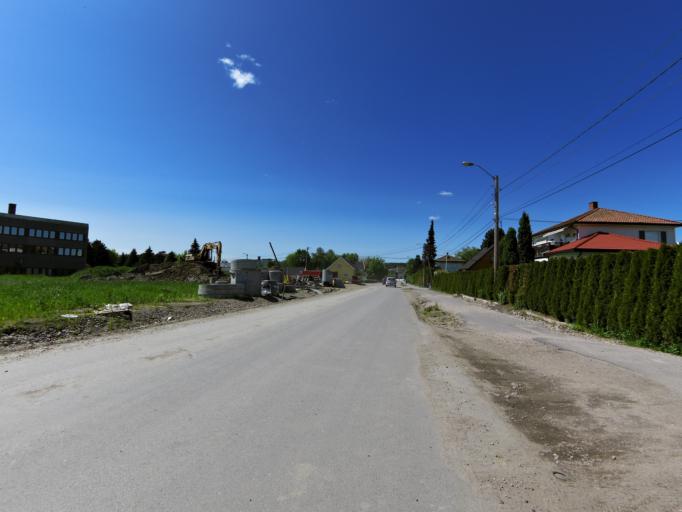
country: NO
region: Ostfold
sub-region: Fredrikstad
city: Fredrikstad
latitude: 59.2329
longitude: 10.9815
